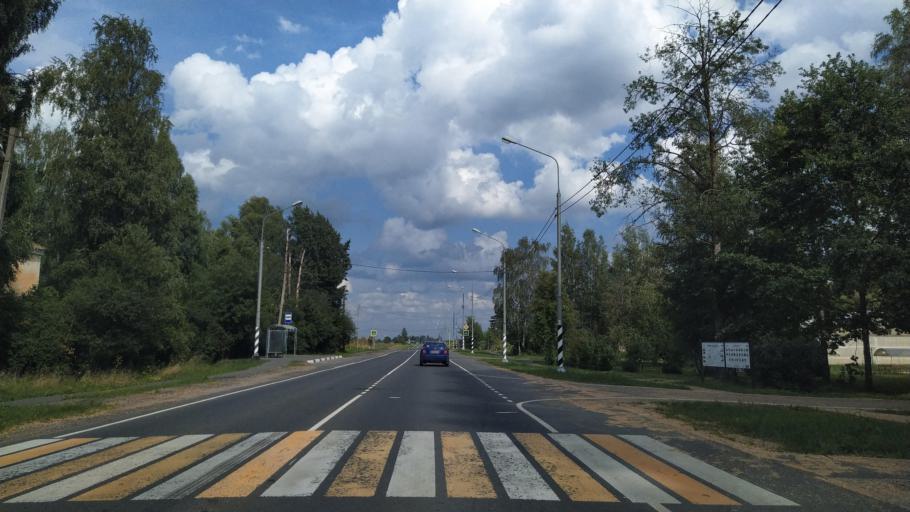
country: RU
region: Novgorod
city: Sol'tsy
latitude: 58.0828
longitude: 30.1107
